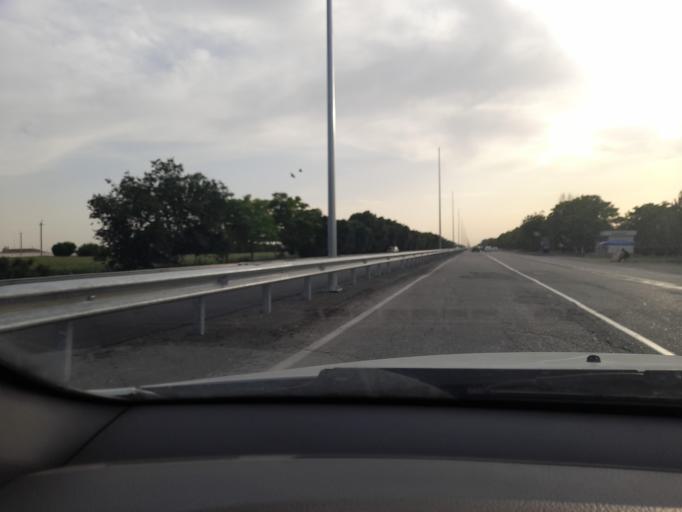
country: UZ
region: Navoiy
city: Konimex
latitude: 40.1291
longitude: 65.1952
